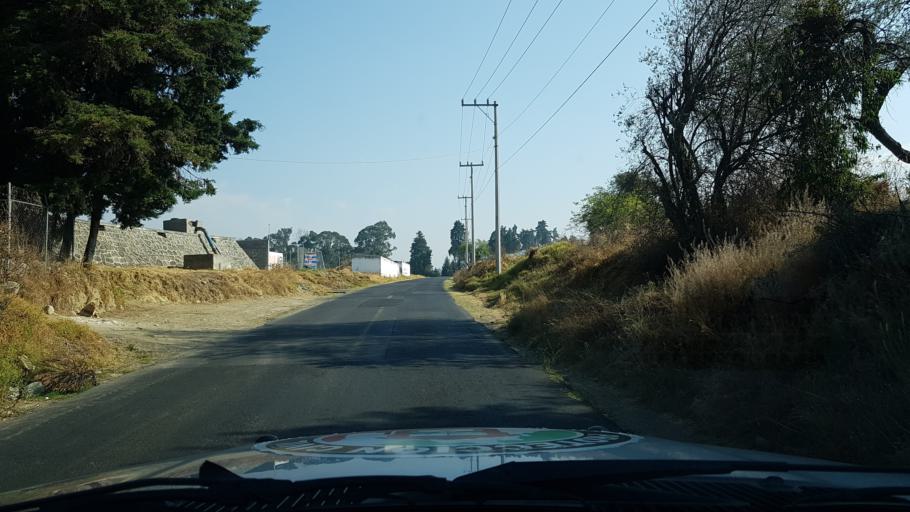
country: MX
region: Mexico
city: Atlautla
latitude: 19.0426
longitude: -98.7739
